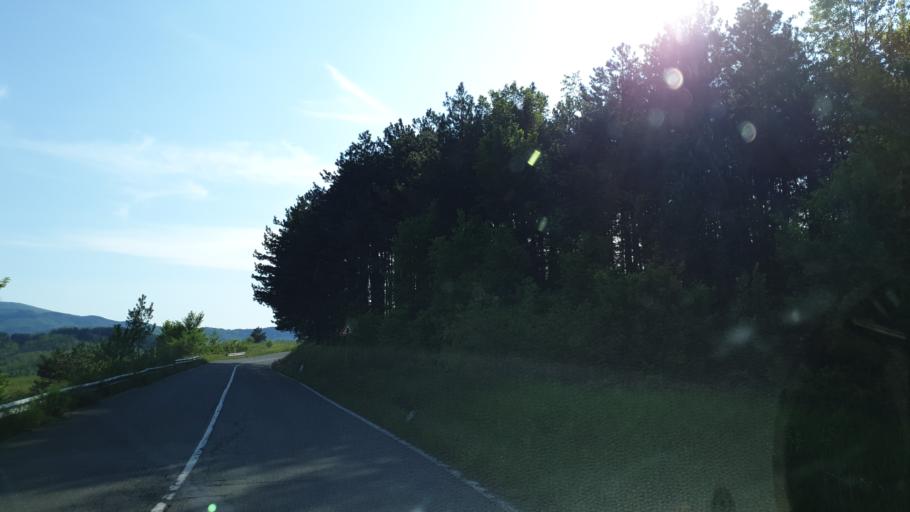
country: IT
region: Tuscany
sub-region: Province of Arezzo
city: Montemignaio
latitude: 43.7875
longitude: 11.6445
